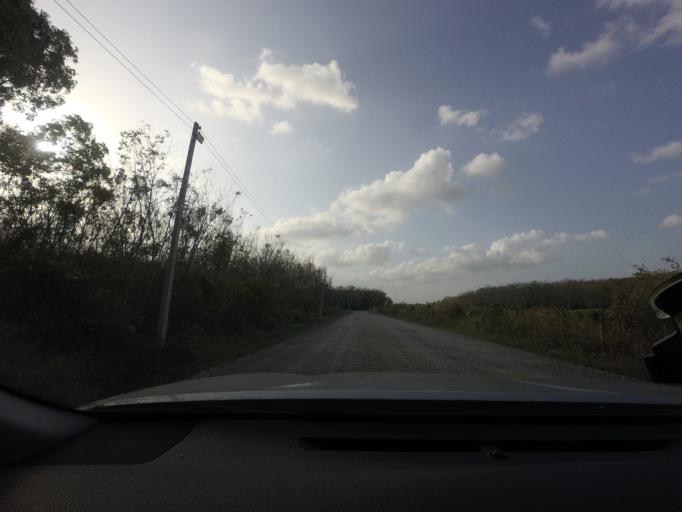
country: TH
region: Pattani
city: Mae Lan
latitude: 6.6207
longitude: 101.2505
